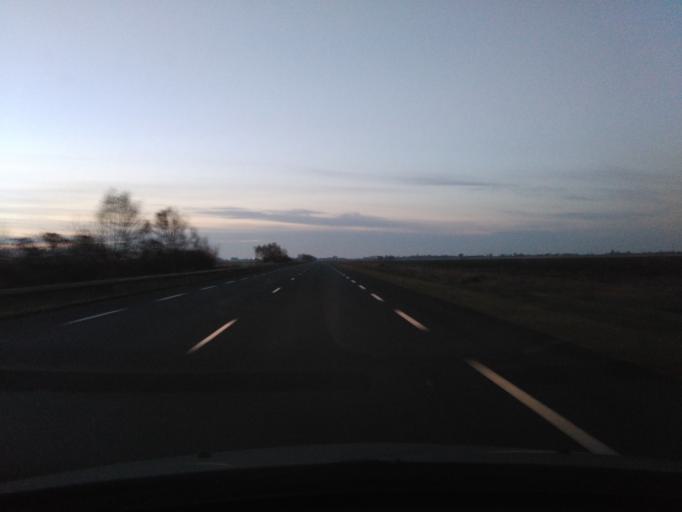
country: FR
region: Pays de la Loire
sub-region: Departement de la Vendee
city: Champagne-les-Marais
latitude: 46.3956
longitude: -1.0951
